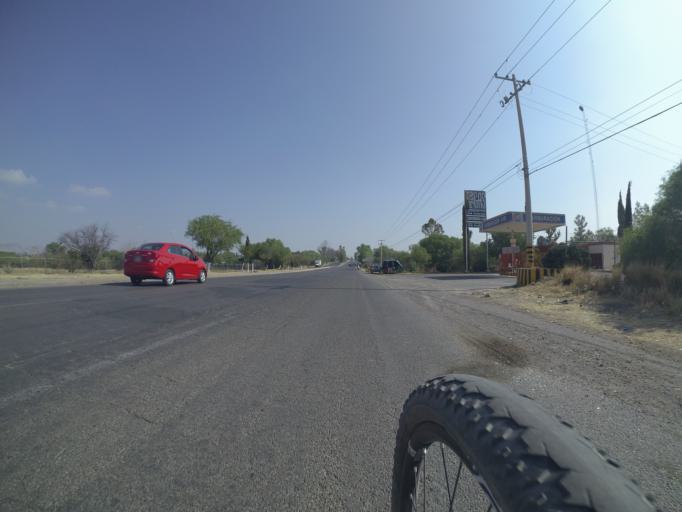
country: MX
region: Aguascalientes
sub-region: Jesus Maria
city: Jesus Maria
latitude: 21.9765
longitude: -102.3387
